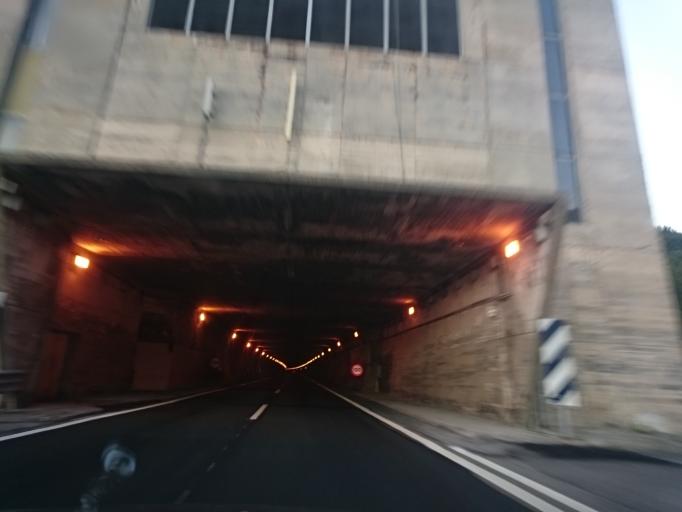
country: ES
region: Castille and Leon
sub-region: Provincia de Leon
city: Sena de Luna
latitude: 42.9783
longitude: -5.8315
